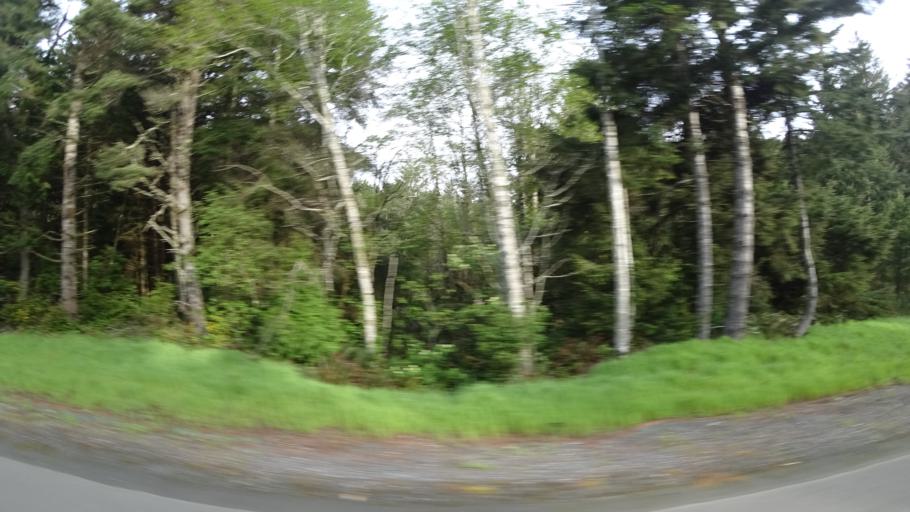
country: US
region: Oregon
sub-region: Coos County
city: Bandon
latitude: 43.1625
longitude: -124.3866
